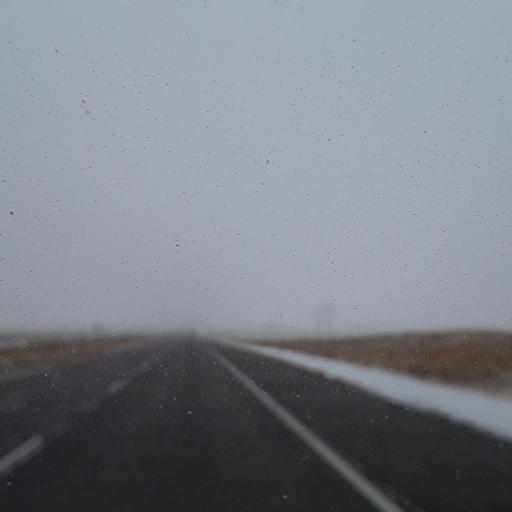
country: US
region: Colorado
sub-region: Logan County
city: Sterling
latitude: 40.7906
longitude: -102.8907
